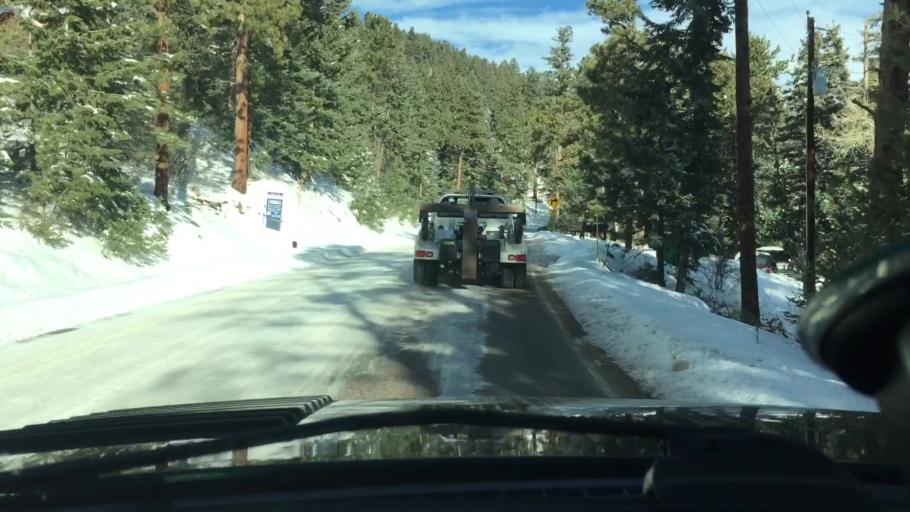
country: US
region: Colorado
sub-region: Jefferson County
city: Indian Hills
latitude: 39.5569
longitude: -105.2472
